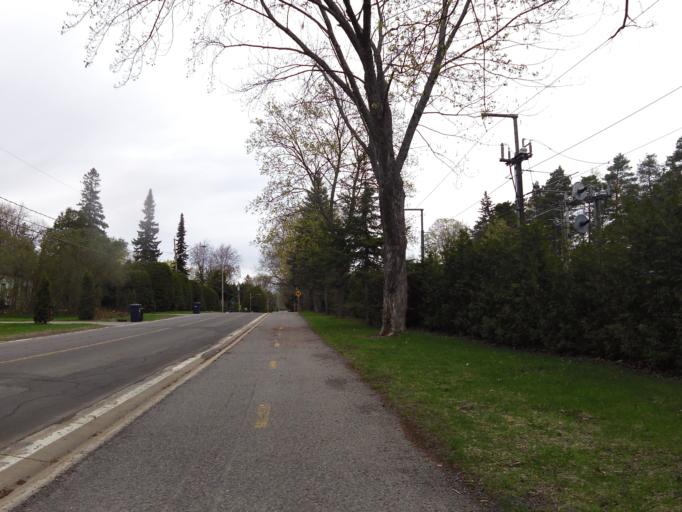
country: CA
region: Quebec
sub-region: Laurentides
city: Deux-Montagnes
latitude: 45.5253
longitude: -73.8749
